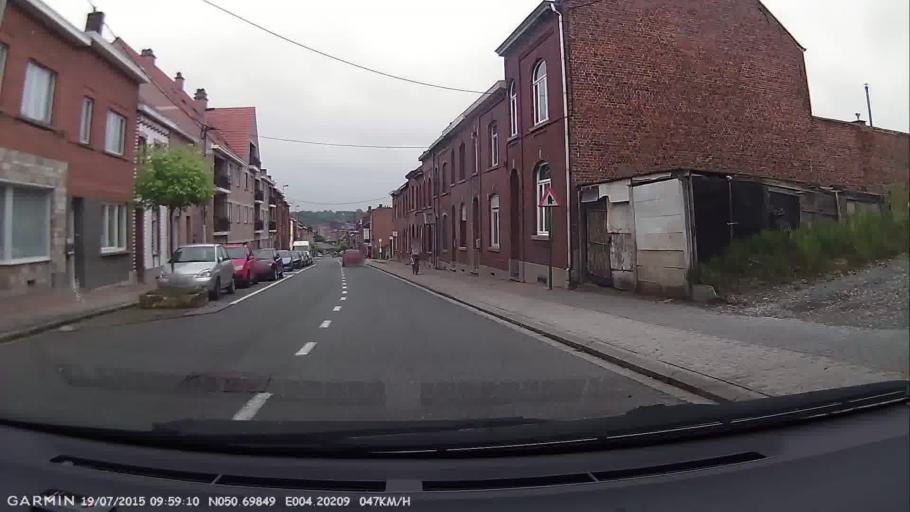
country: BE
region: Wallonia
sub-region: Province du Brabant Wallon
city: Tubize
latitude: 50.6984
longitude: 4.2021
